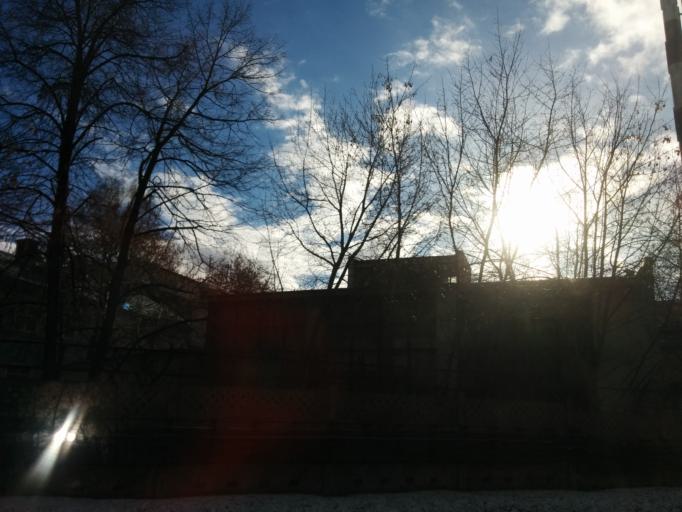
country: RU
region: Moscow
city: Vorob'yovo
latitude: 55.7437
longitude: 37.5198
